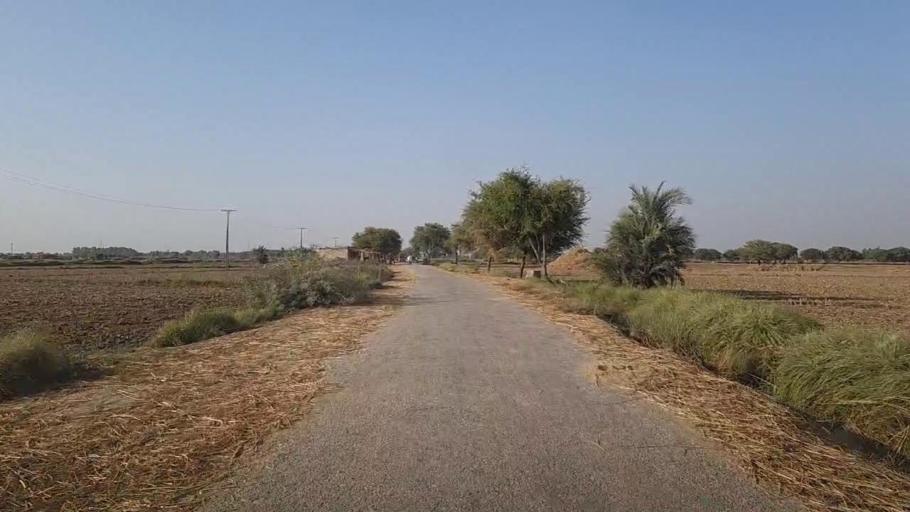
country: PK
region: Sindh
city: Kashmor
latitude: 28.4148
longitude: 69.4109
